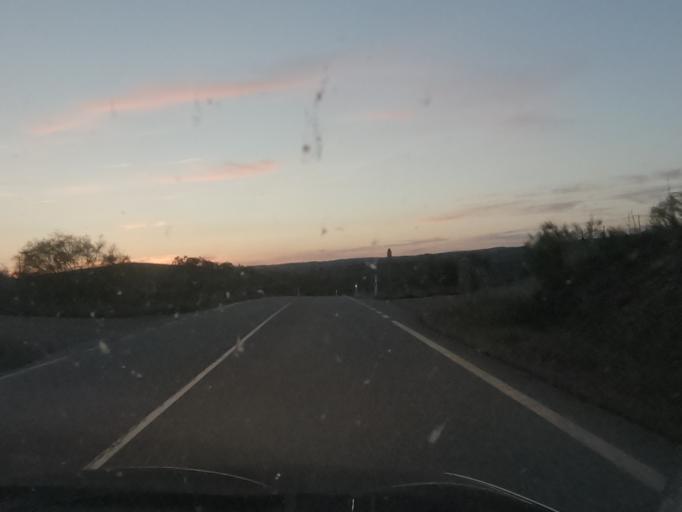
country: ES
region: Extremadura
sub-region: Provincia de Caceres
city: Piedras Albas
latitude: 39.8045
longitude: -6.9733
